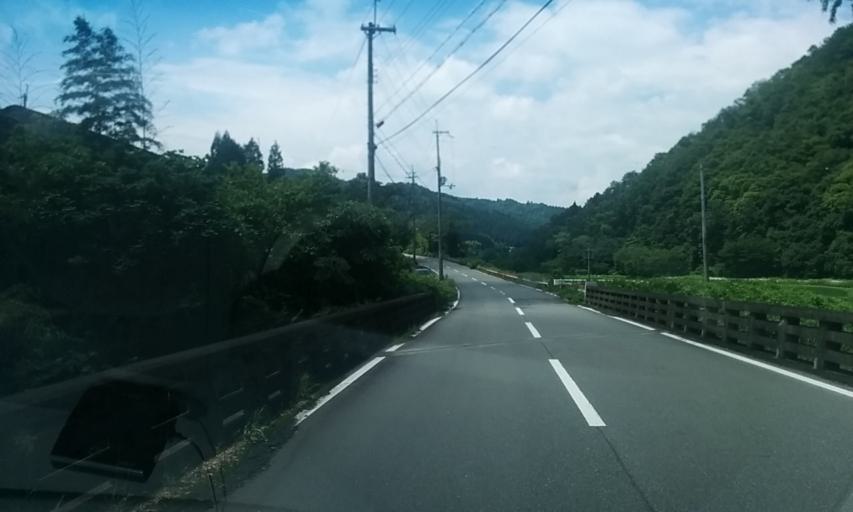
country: JP
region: Hyogo
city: Sasayama
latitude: 35.1678
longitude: 135.2713
